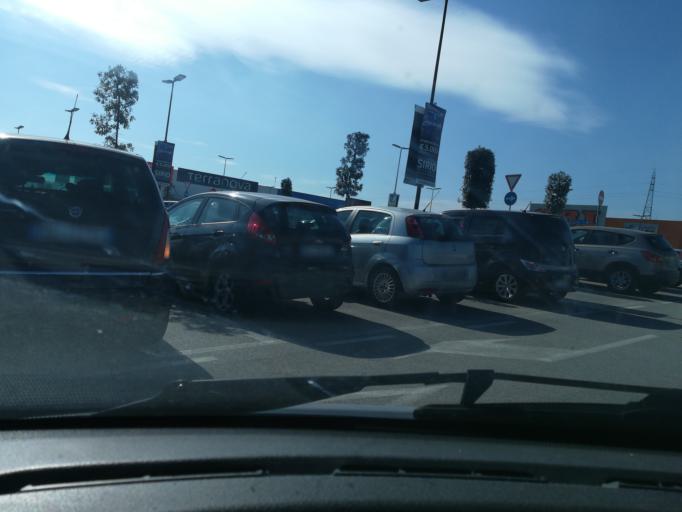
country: IT
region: The Marches
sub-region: Provincia di Macerata
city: Santa Maria Apparente
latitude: 43.2929
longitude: 13.7029
